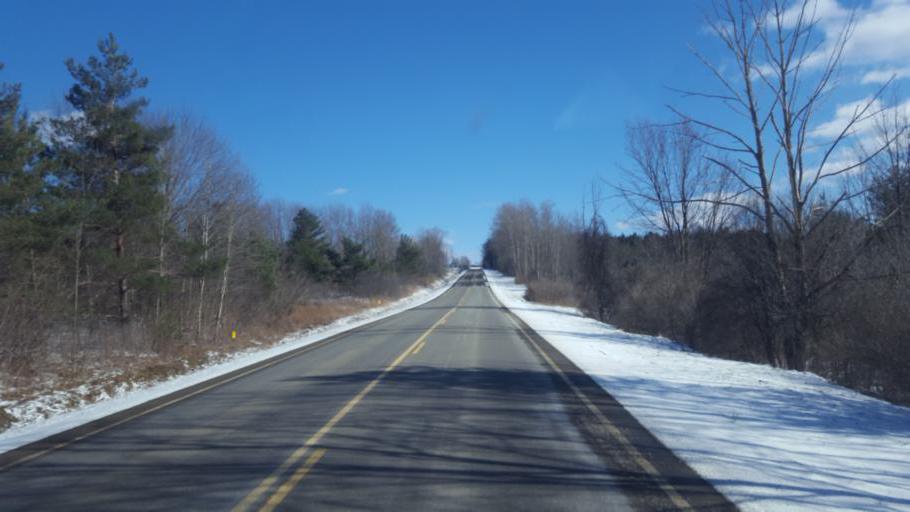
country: US
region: New York
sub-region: Allegany County
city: Friendship
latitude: 42.2003
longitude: -78.1073
